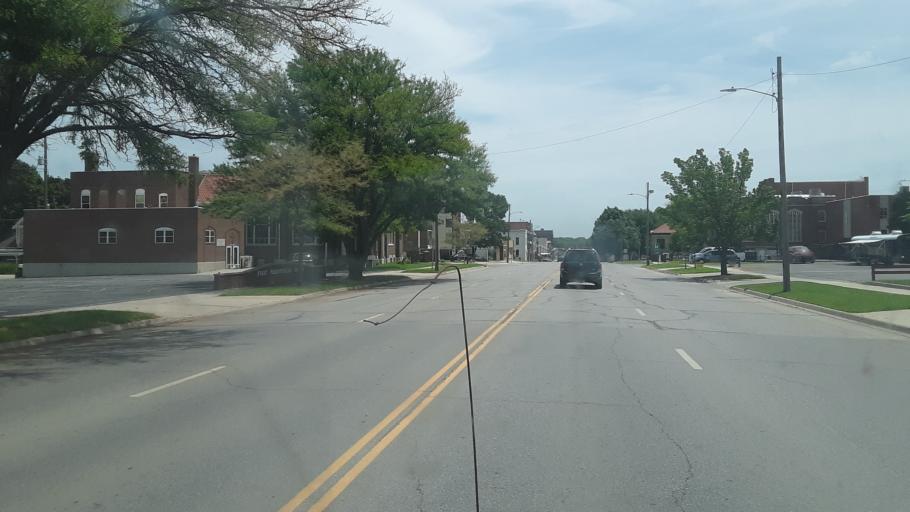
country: US
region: Kansas
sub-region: Butler County
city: El Dorado
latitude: 37.8174
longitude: -96.8553
